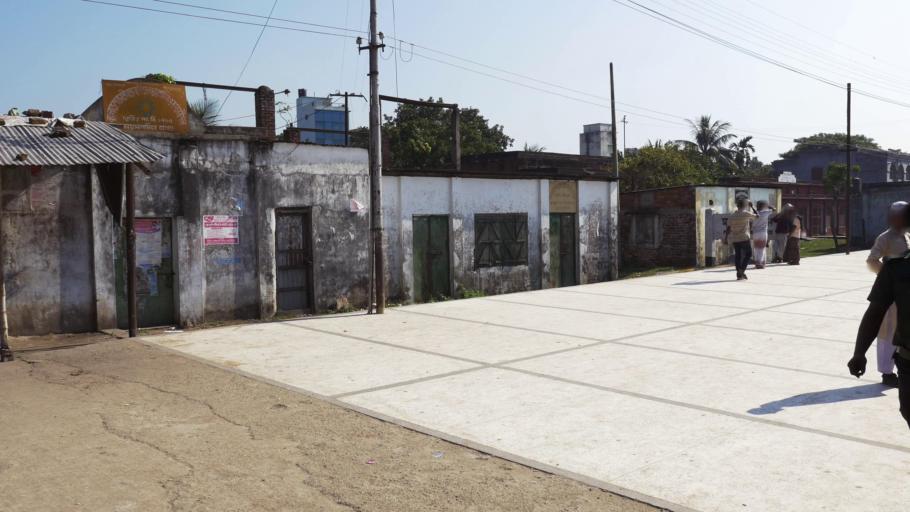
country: BD
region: Dhaka
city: Mymensingh
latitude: 24.6914
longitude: 90.4542
